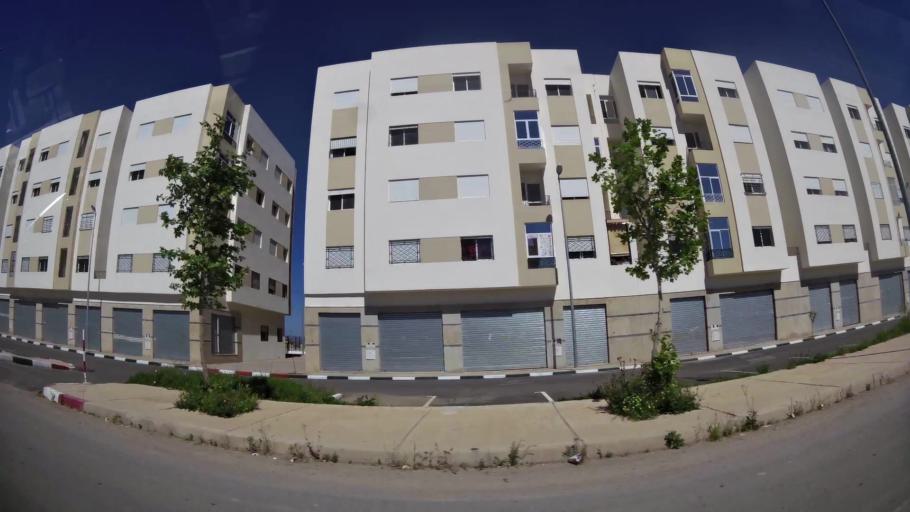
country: MA
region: Oriental
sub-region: Oujda-Angad
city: Oujda
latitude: 34.6719
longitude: -1.8594
